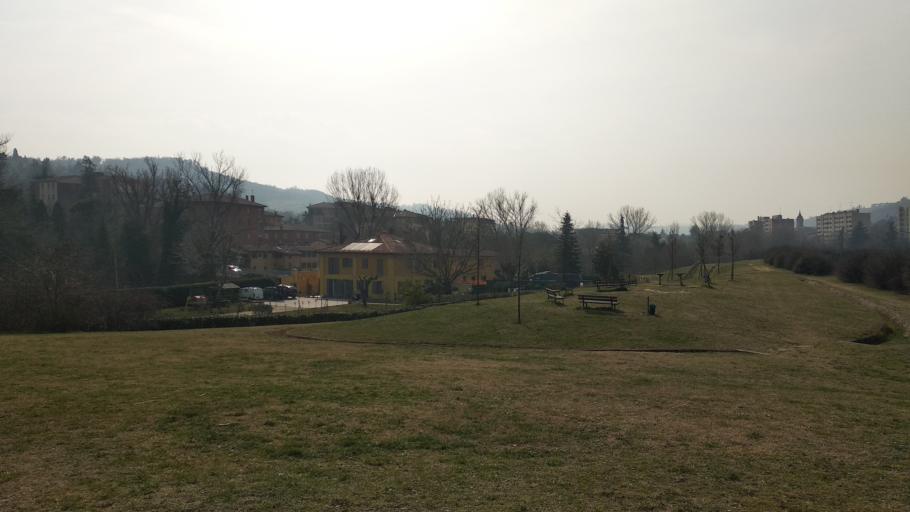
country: IT
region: Emilia-Romagna
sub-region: Provincia di Bologna
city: Ponticella
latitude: 44.4611
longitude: 11.3788
